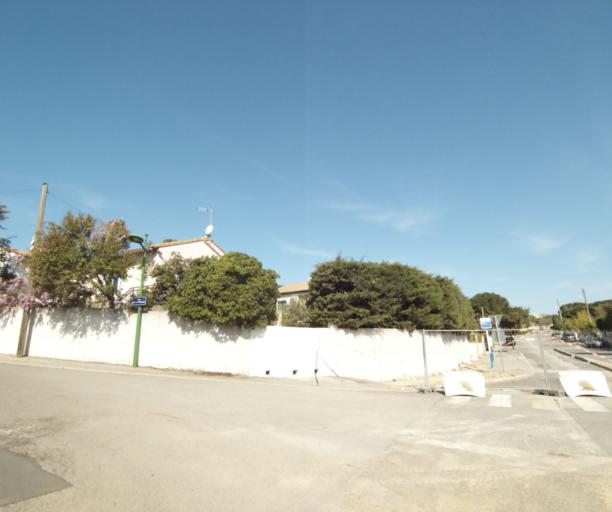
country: FR
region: Languedoc-Roussillon
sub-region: Departement de l'Herault
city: Le Cres
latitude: 43.6450
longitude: 3.9349
